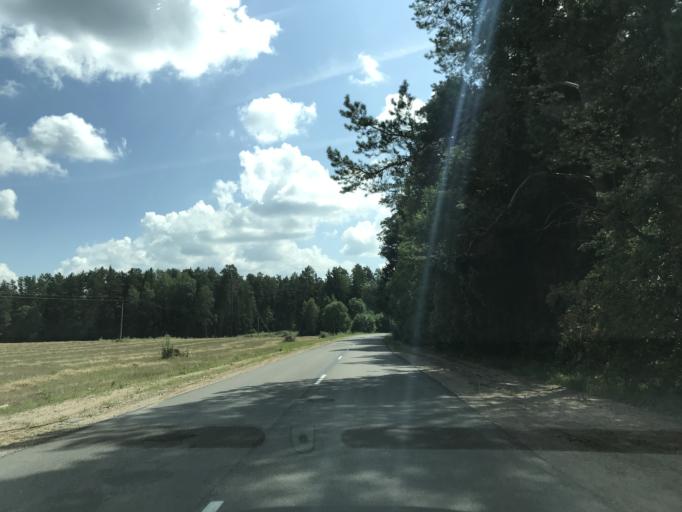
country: BY
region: Minsk
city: Rakaw
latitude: 54.0051
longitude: 26.9834
